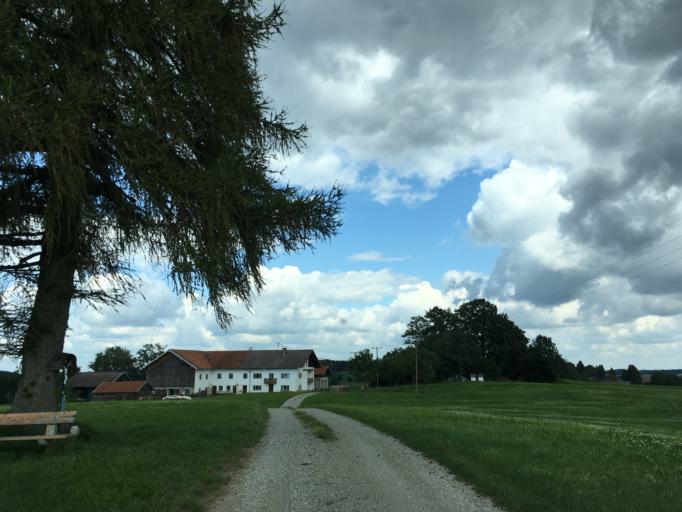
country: DE
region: Bavaria
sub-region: Upper Bavaria
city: Pittenhart
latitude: 48.0196
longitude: 12.3676
